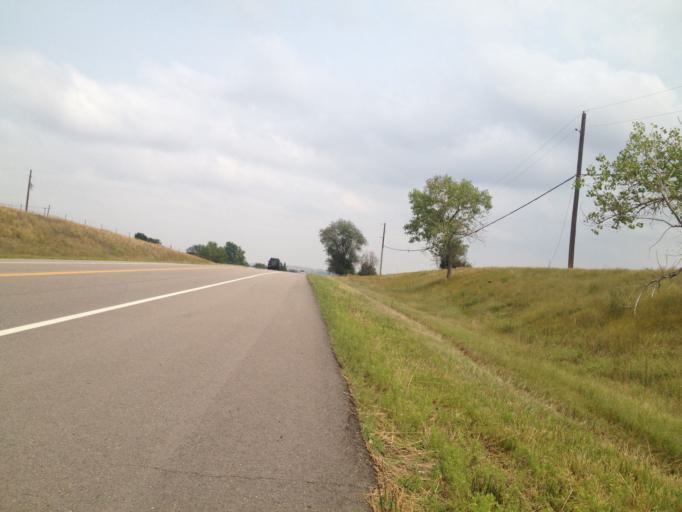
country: US
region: Colorado
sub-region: Boulder County
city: Louisville
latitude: 39.9726
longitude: -105.1171
